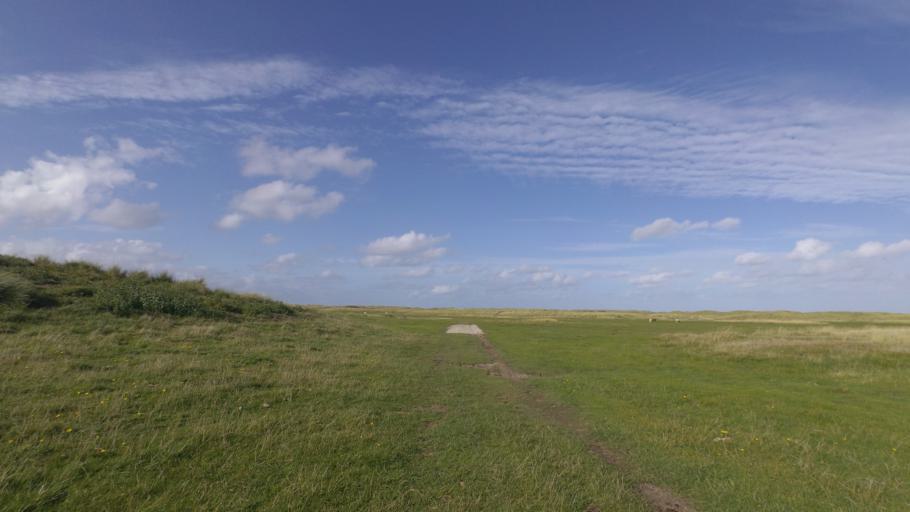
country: NL
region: Friesland
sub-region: Gemeente Ameland
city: Nes
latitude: 53.4525
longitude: 5.8622
